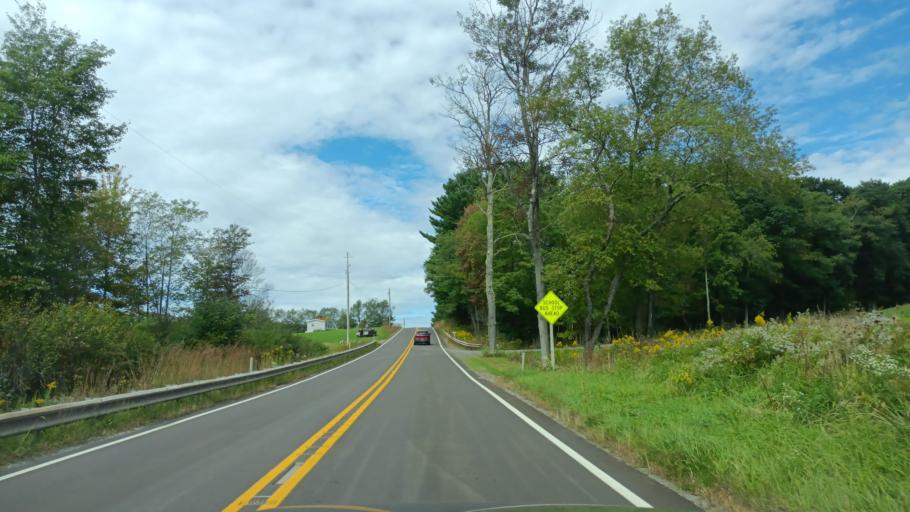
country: US
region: Maryland
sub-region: Garrett County
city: Oakland
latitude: 39.3106
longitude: -79.4756
